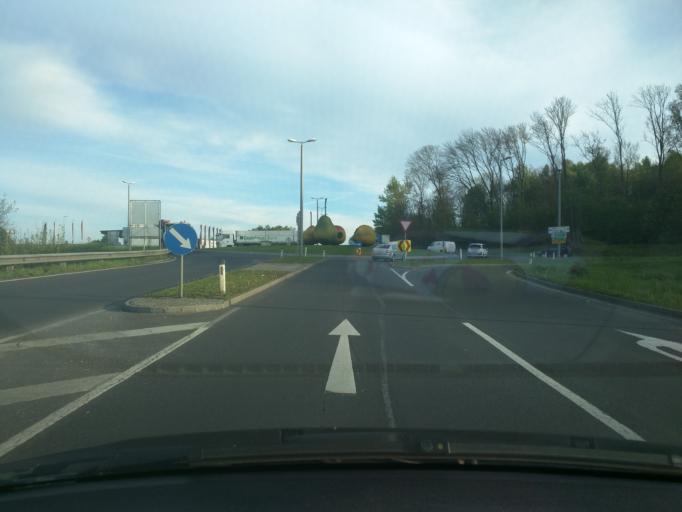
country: AT
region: Lower Austria
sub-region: Politischer Bezirk Amstetten
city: Amstetten
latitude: 48.1327
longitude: 14.8391
